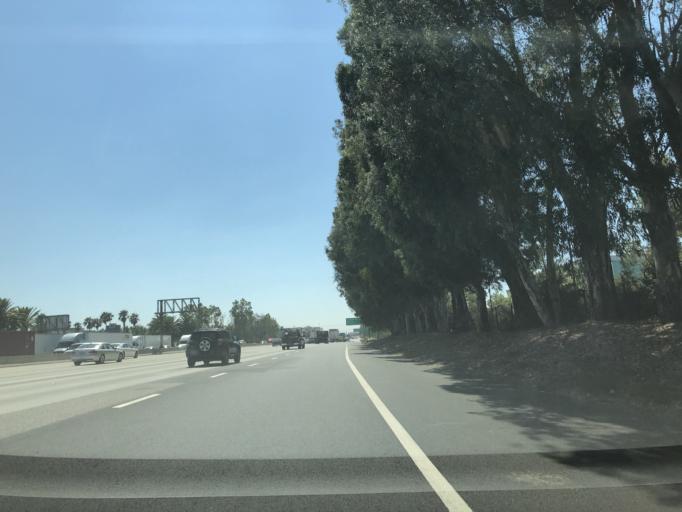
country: US
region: California
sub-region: San Bernardino County
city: Rancho Cucamonga
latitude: 34.0679
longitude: -117.5789
